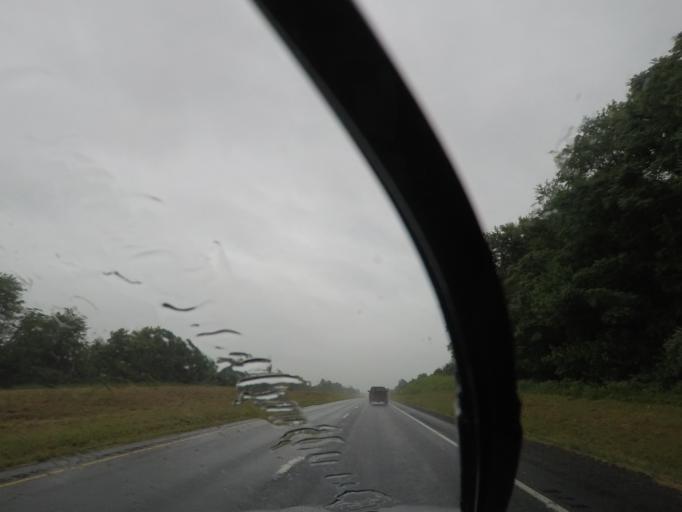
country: US
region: Virginia
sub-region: Culpeper County
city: Culpeper
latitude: 38.4645
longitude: -77.9624
